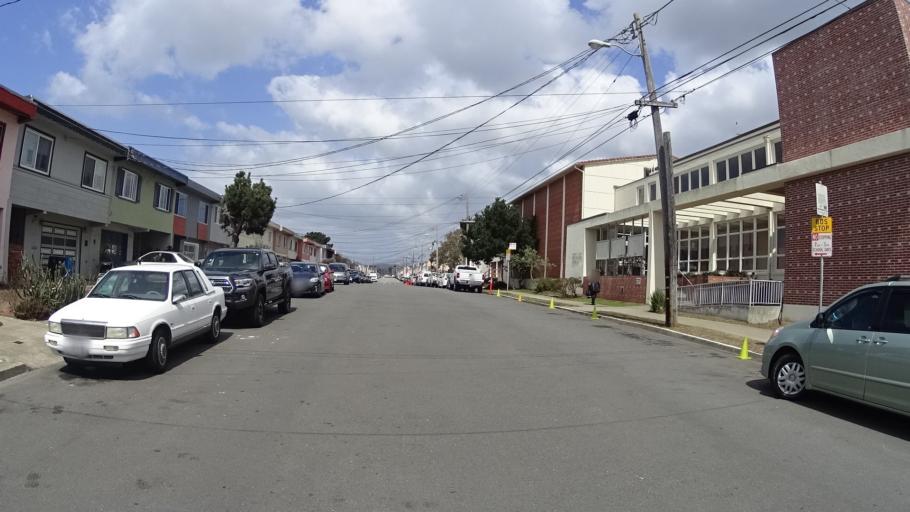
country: US
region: California
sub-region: San Mateo County
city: Daly City
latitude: 37.7484
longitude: -122.4933
